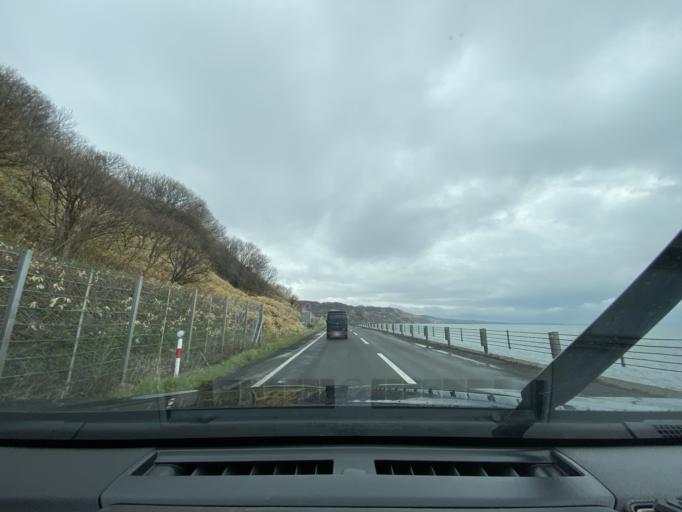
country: JP
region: Hokkaido
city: Ishikari
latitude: 43.4270
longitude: 141.4230
